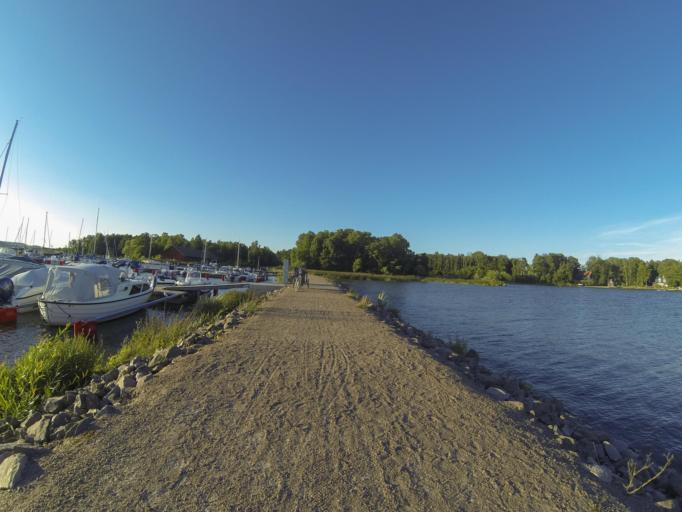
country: SE
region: Vaestmanland
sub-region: Vasteras
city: Vasteras
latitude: 59.5471
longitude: 16.6584
